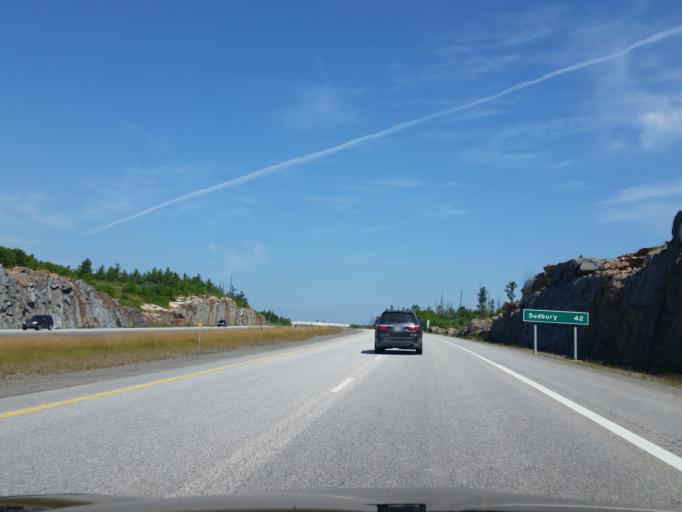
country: CA
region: Ontario
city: Greater Sudbury
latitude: 46.2322
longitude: -80.7753
